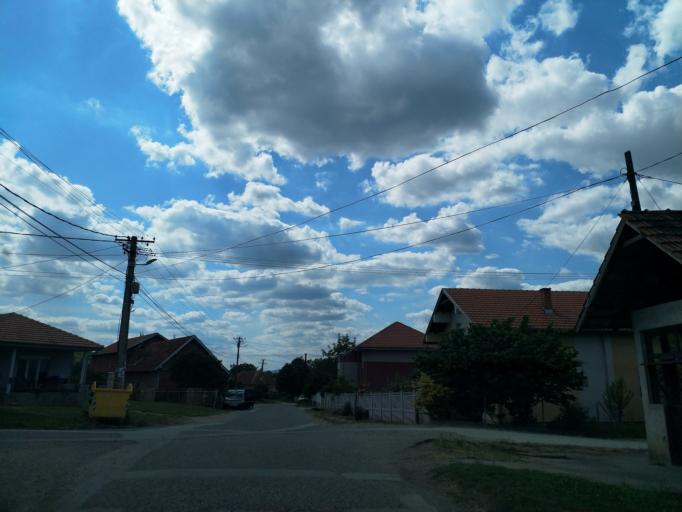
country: RS
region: Central Serbia
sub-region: Pomoravski Okrug
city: Jagodina
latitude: 43.9402
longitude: 21.3045
